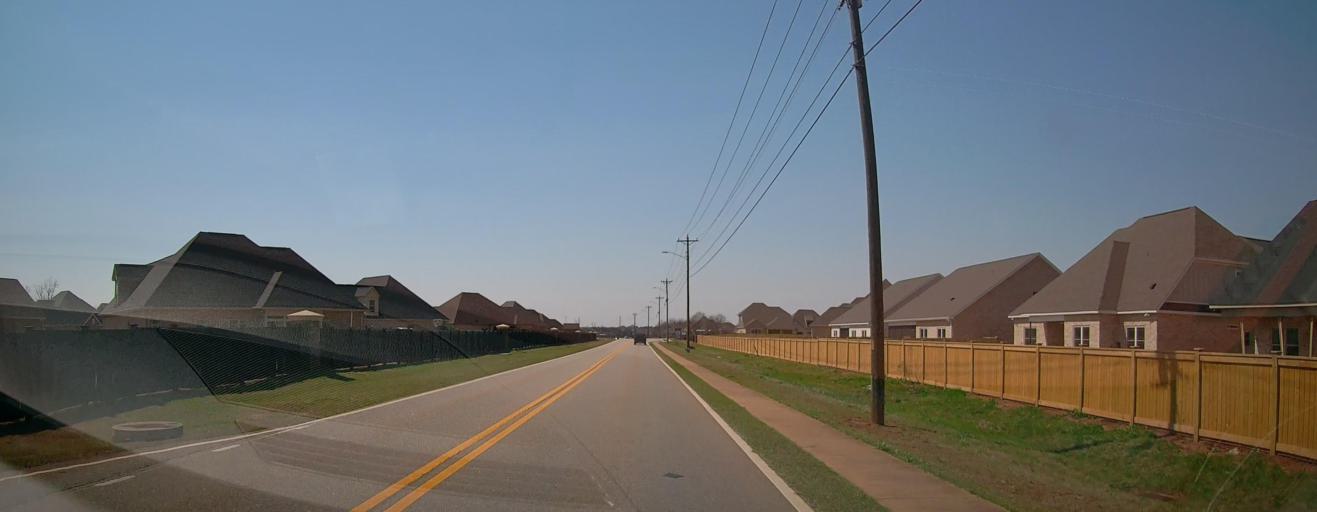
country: US
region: Georgia
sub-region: Houston County
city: Centerville
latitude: 32.5699
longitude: -83.7050
